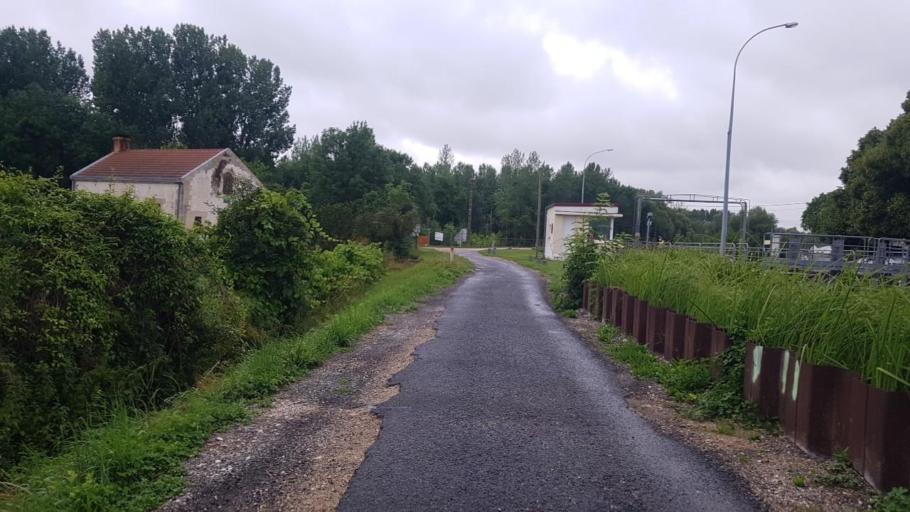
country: FR
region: Champagne-Ardenne
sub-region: Departement de la Marne
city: Vitry-le-Francois
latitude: 48.7491
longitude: 4.5725
